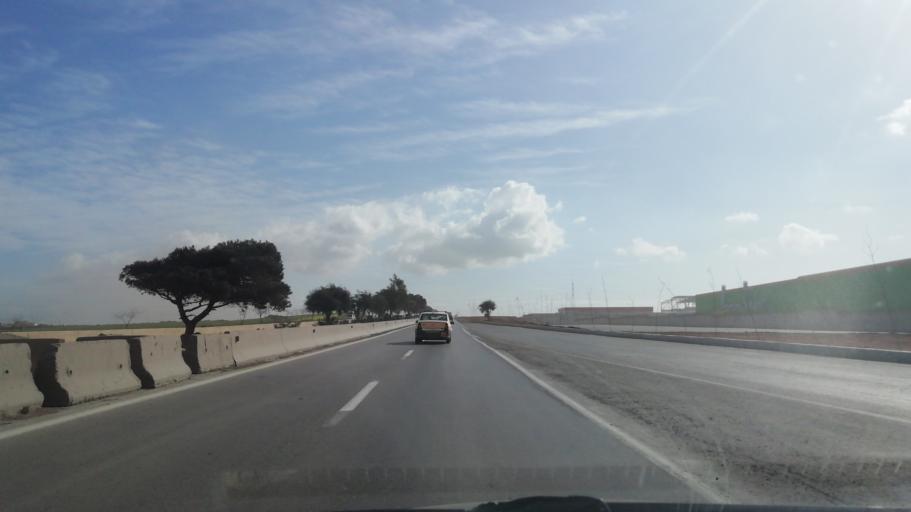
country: DZ
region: Oran
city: Ain el Bya
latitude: 35.7748
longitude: -0.2536
